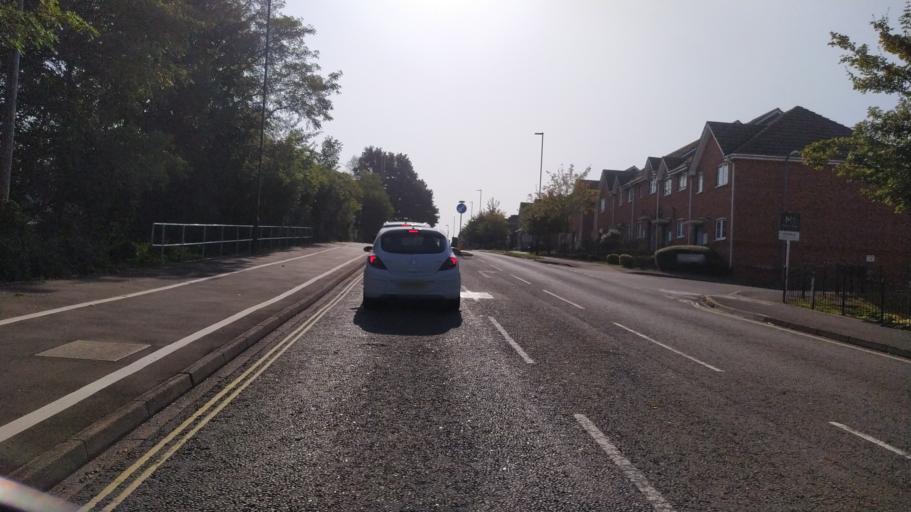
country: GB
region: England
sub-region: Hampshire
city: West End
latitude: 50.9095
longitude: -1.3480
